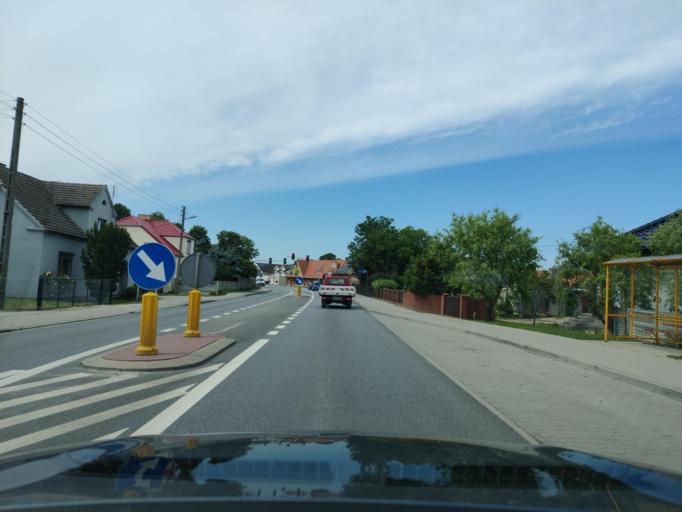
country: PL
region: Greater Poland Voivodeship
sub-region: Powiat grodziski
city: Granowo
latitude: 52.2467
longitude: 16.6142
